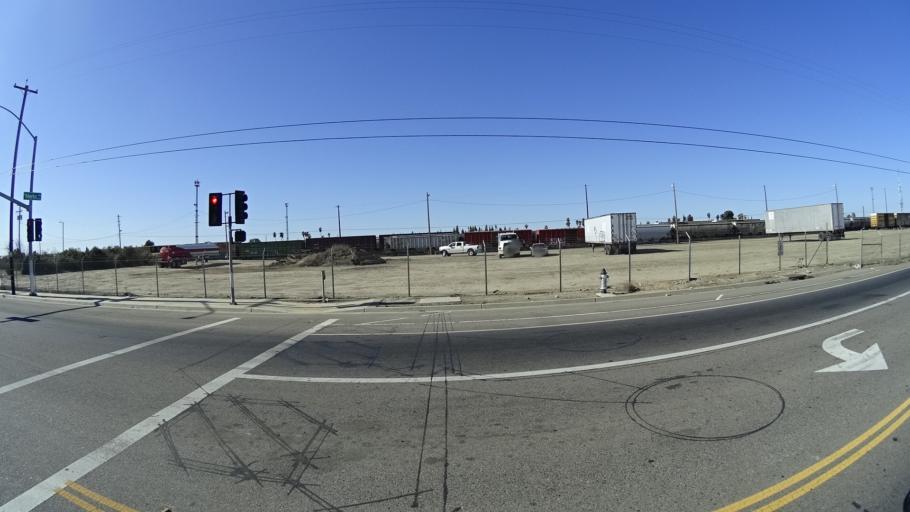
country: US
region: California
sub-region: Fresno County
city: West Park
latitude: 36.7817
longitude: -119.8446
